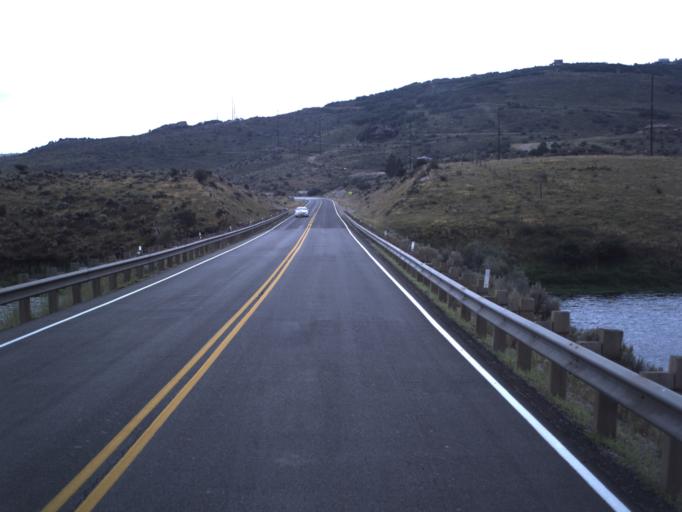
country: US
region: Utah
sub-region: Summit County
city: Oakley
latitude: 40.7763
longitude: -111.4086
